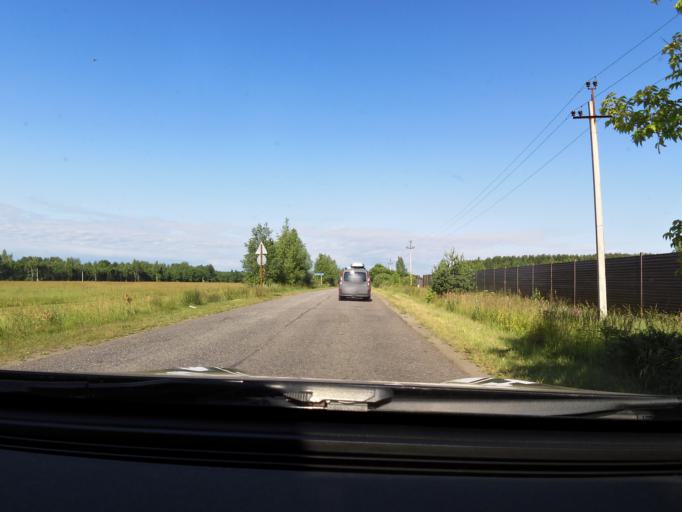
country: RU
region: Tverskaya
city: Zavidovo
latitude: 56.6084
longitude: 36.5876
